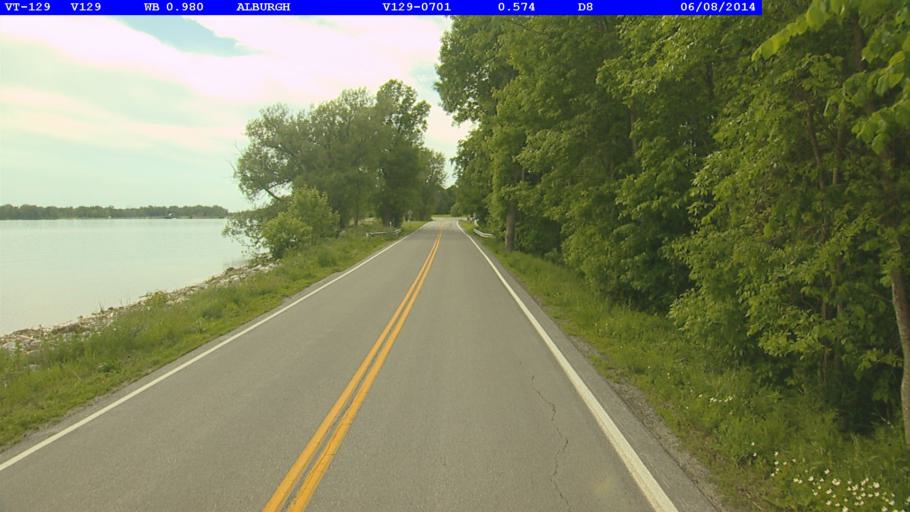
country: US
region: Vermont
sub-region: Grand Isle County
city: North Hero
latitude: 44.9031
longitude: -73.3049
